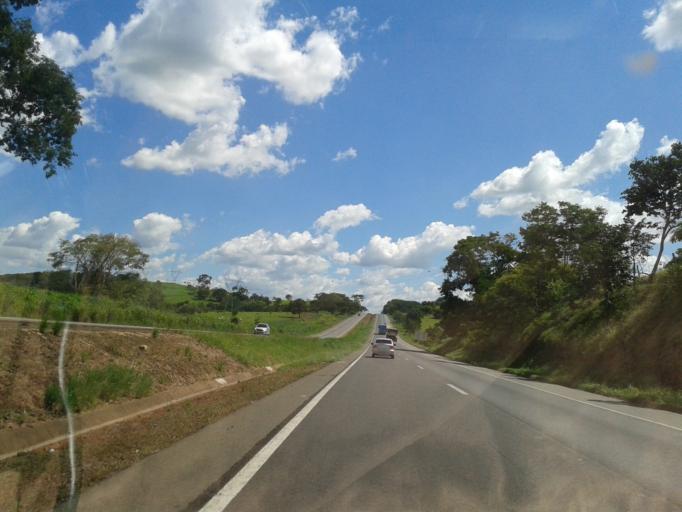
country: BR
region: Goias
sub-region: Piracanjuba
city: Piracanjuba
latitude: -17.4169
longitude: -49.2264
